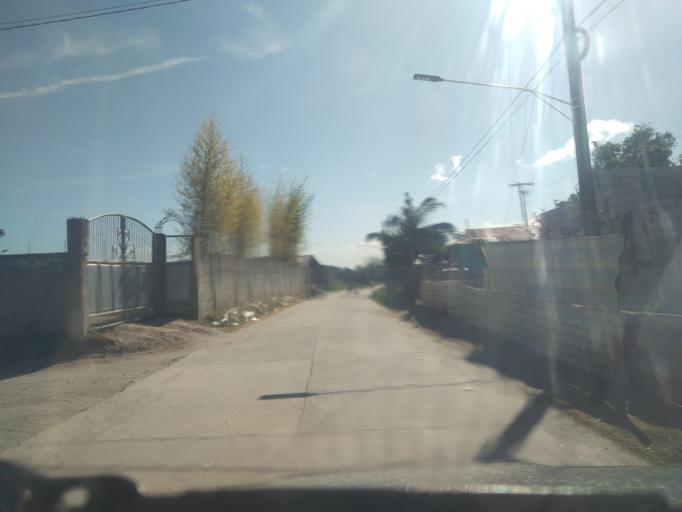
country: PH
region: Central Luzon
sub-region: Province of Pampanga
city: Calibutbut
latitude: 15.0923
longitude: 120.5947
